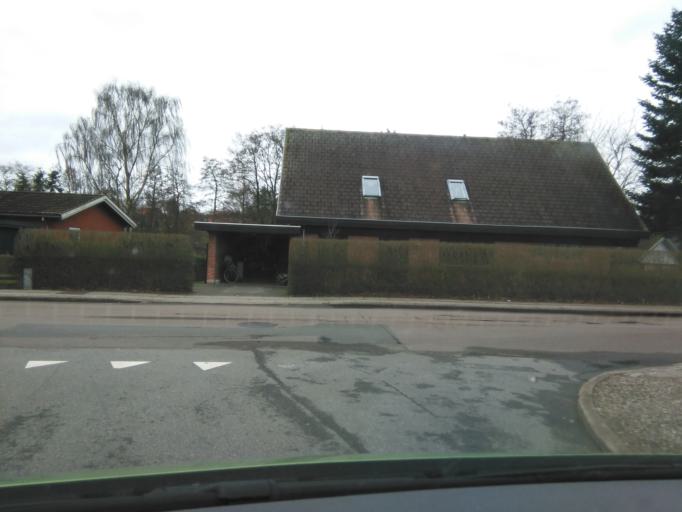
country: DK
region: Central Jutland
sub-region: Odder Kommune
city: Odder
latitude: 55.9814
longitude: 10.1481
